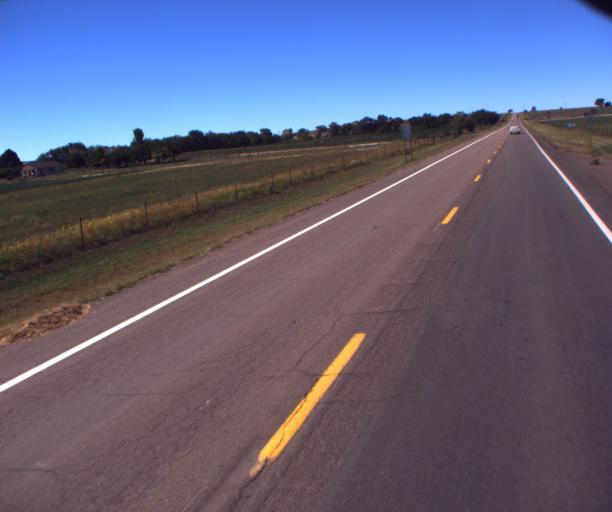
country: US
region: Arizona
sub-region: Apache County
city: Saint Johns
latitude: 34.5063
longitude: -109.3954
